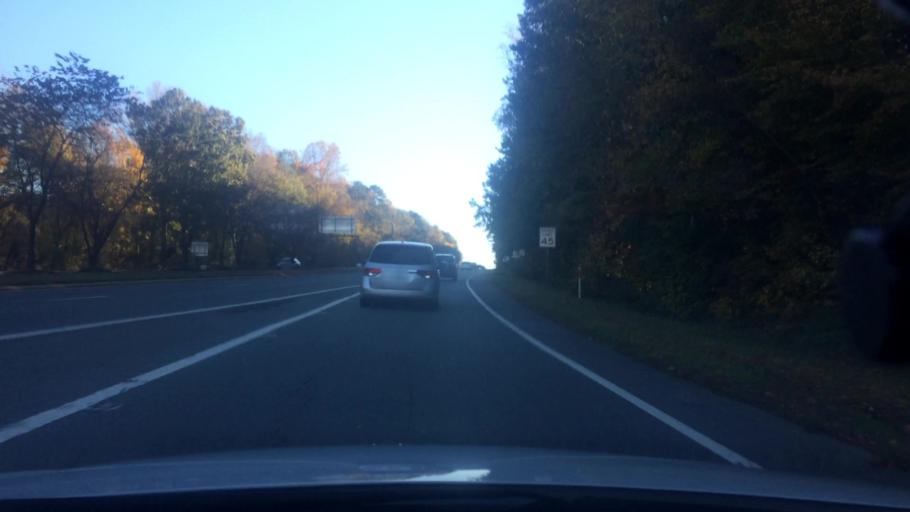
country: US
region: North Carolina
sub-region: Orange County
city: Chapel Hill
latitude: 35.8938
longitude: -79.0552
